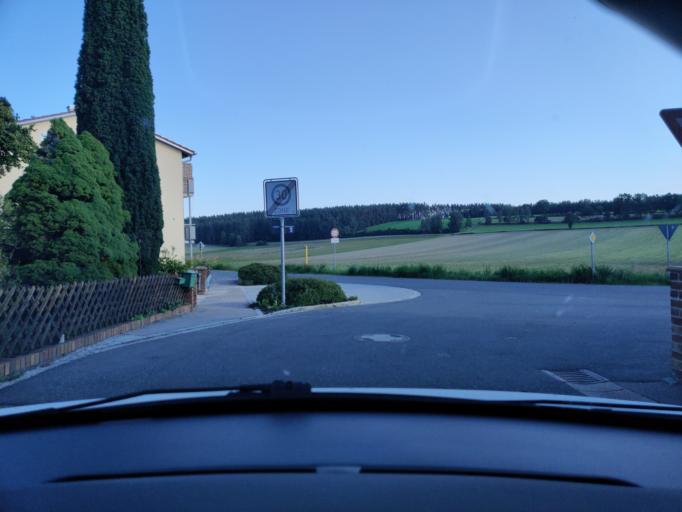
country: DE
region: Bavaria
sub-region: Upper Palatinate
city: Stulln
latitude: 49.4210
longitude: 12.1502
